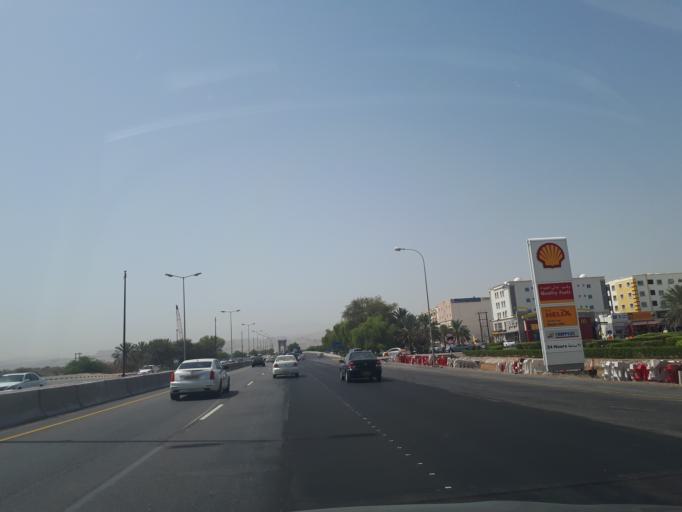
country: OM
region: Muhafazat Masqat
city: As Sib al Jadidah
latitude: 23.5971
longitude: 58.2503
